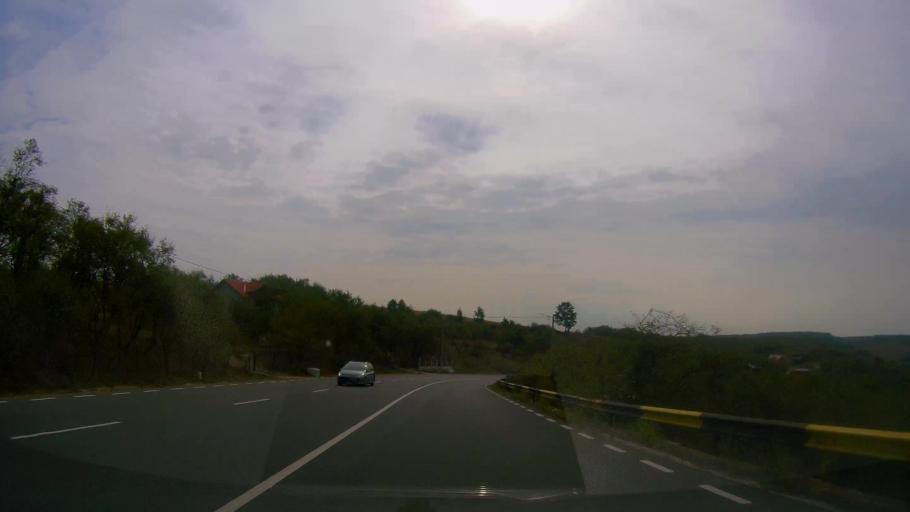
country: RO
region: Salaj
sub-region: Comuna Treznea
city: Treznea
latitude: 47.1334
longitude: 23.1296
